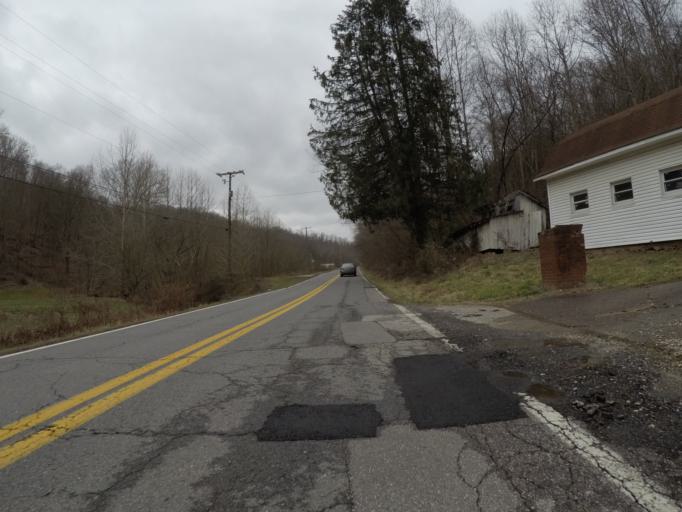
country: US
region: West Virginia
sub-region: Cabell County
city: Lesage
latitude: 38.4700
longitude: -82.2857
